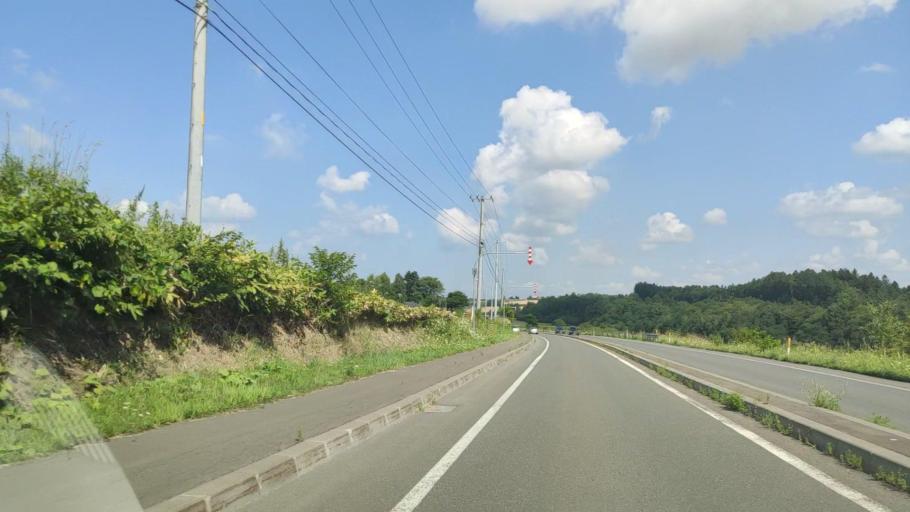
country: JP
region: Hokkaido
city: Shimo-furano
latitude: 43.5258
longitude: 142.4461
